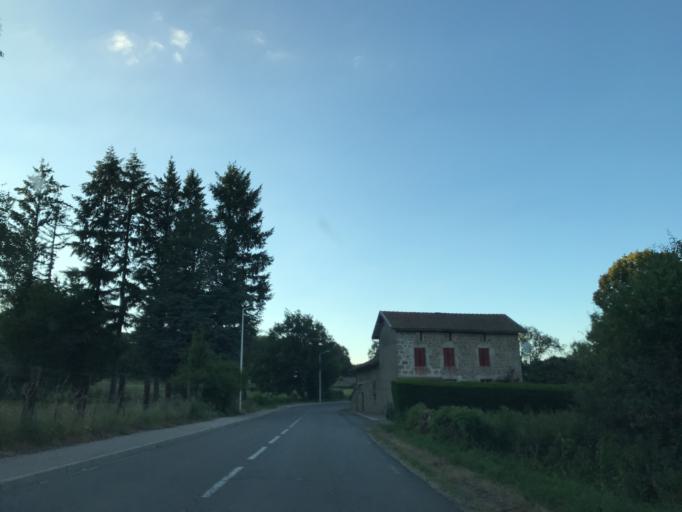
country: FR
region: Rhone-Alpes
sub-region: Departement de la Loire
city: Noiretable
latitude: 45.8083
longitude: 3.7692
